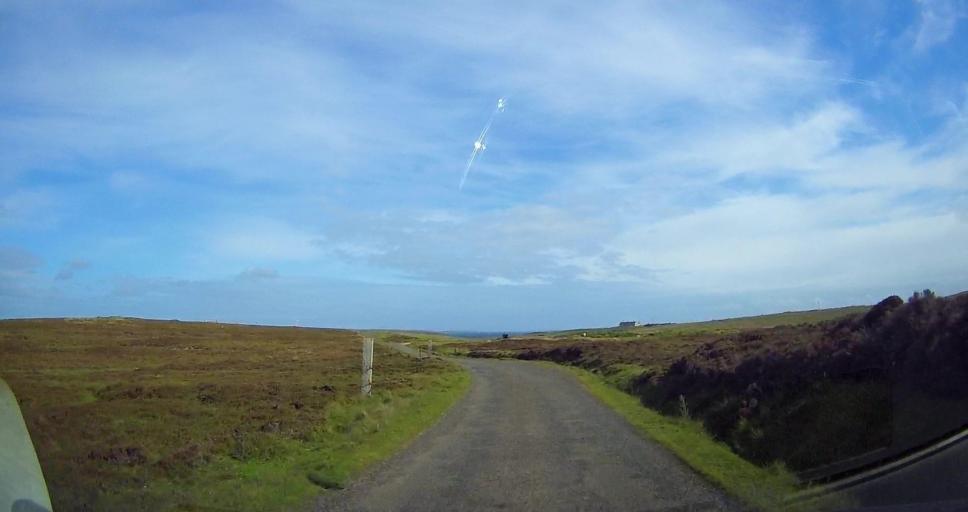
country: GB
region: Scotland
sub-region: Orkney Islands
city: Stromness
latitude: 58.8552
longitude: -3.2117
